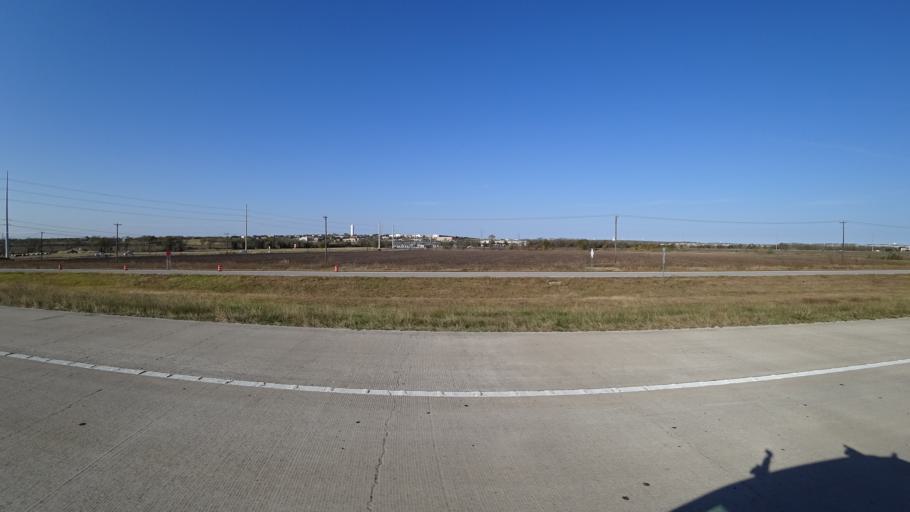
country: US
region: Texas
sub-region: Travis County
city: Pflugerville
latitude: 30.4545
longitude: -97.5946
